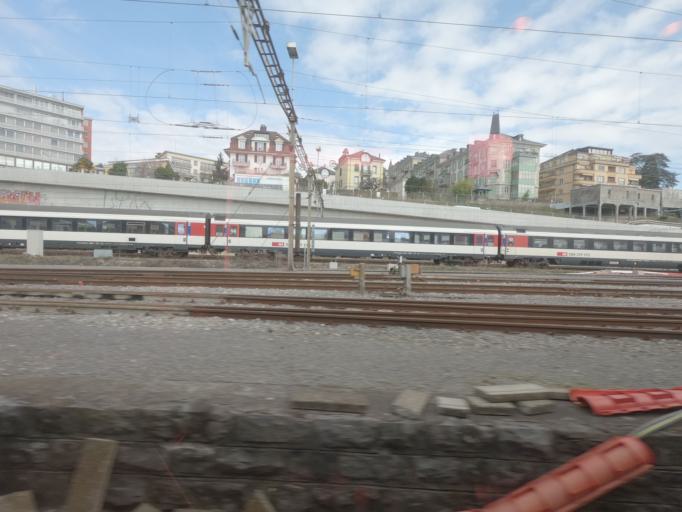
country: CH
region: Vaud
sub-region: Lausanne District
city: Lausanne
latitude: 46.5185
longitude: 6.6203
